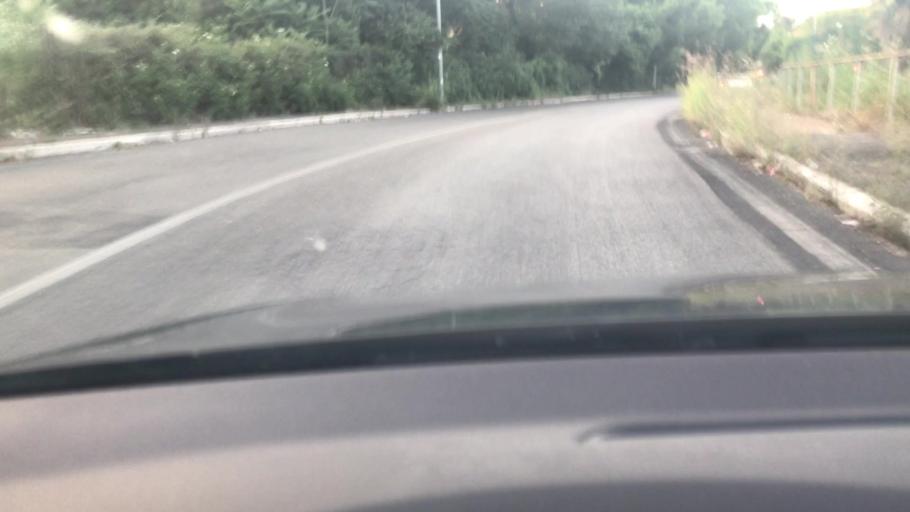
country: IT
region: Latium
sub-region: Citta metropolitana di Roma Capitale
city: Rome
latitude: 41.9267
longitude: 12.5635
